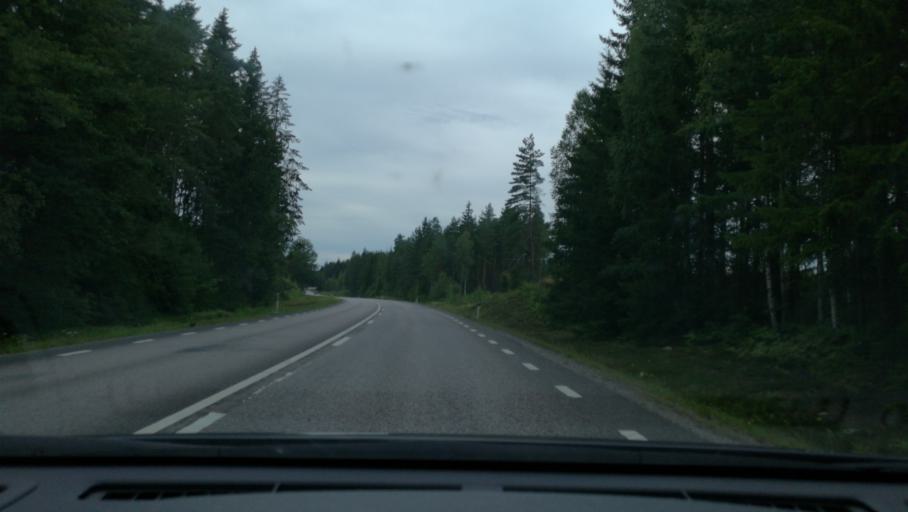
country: SE
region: Soedermanland
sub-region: Katrineholms Kommun
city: Katrineholm
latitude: 59.0730
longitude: 16.2205
